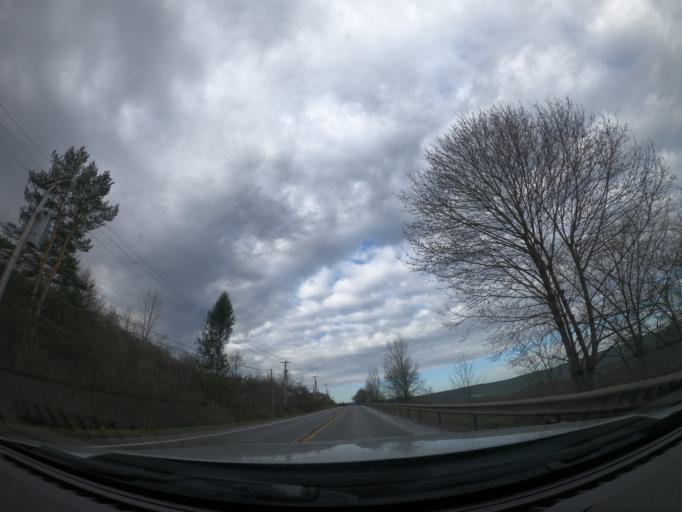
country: US
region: New York
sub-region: Madison County
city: Cazenovia
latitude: 42.7477
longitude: -75.9307
